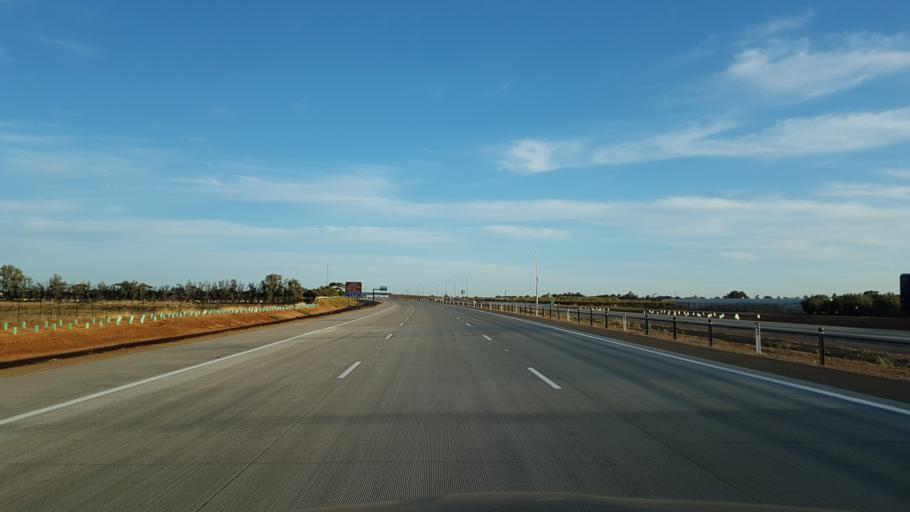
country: AU
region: South Australia
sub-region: Salisbury
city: Salisbury
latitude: -34.7441
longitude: 138.5801
